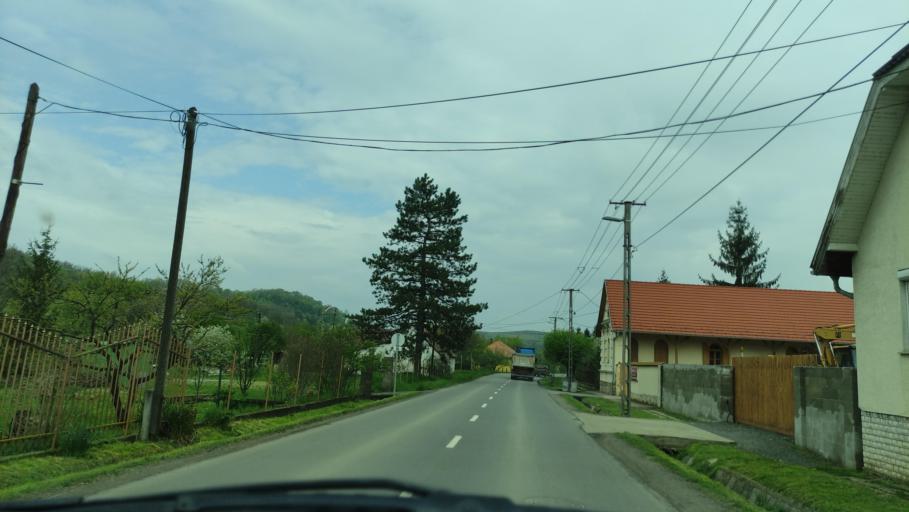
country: HU
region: Baranya
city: Komlo
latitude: 46.2139
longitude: 18.2429
